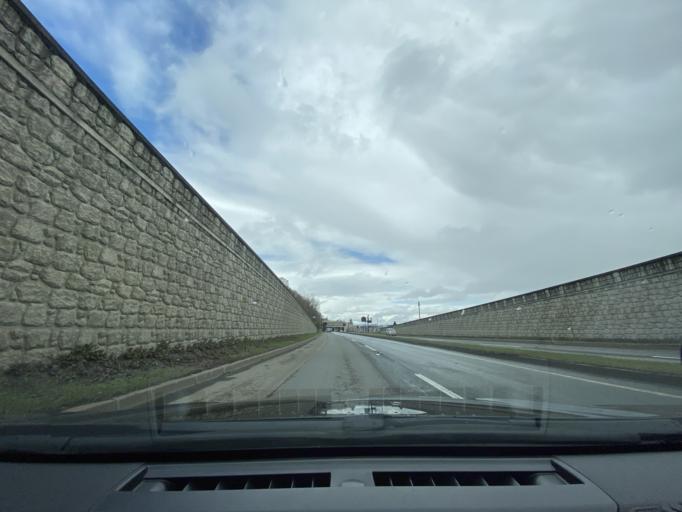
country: JP
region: Hokkaido
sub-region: Asahikawa-shi
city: Asahikawa
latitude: 43.8060
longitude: 142.3552
